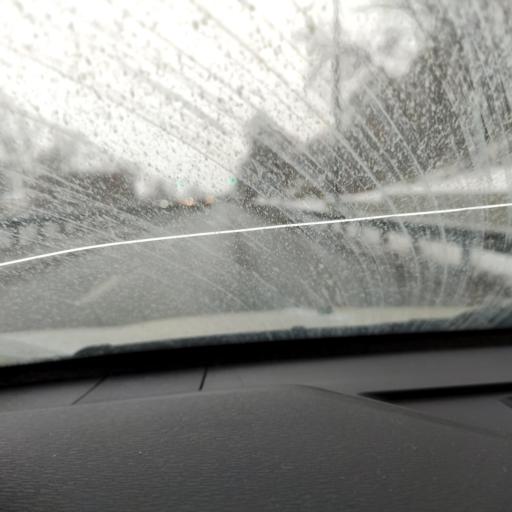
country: RU
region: Samara
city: Volzhskiy
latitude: 53.3925
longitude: 50.1563
